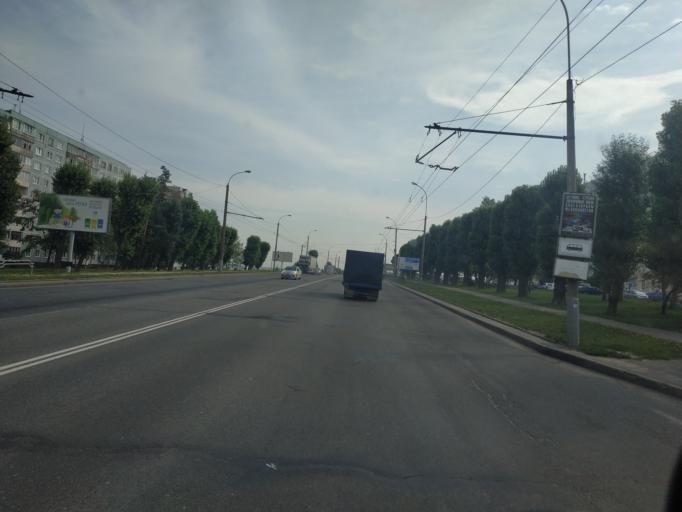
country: BY
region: Mogilev
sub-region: Mahilyowski Rayon
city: Veyno
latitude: 53.8759
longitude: 30.3787
